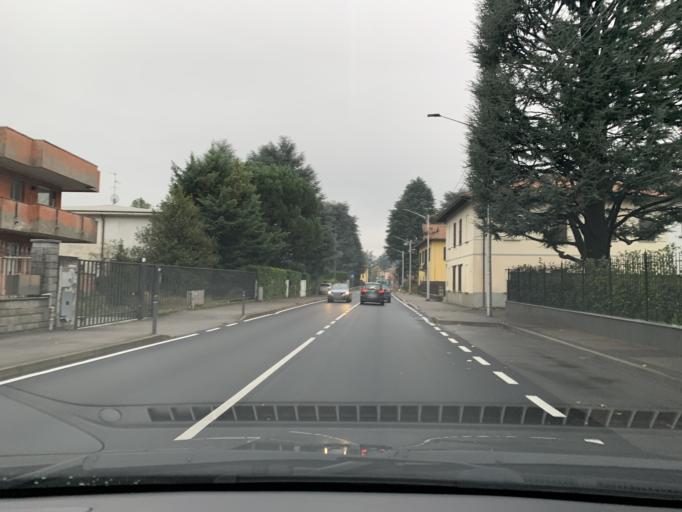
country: IT
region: Lombardy
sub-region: Provincia di Como
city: Rovellasca
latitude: 45.6725
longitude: 9.0538
